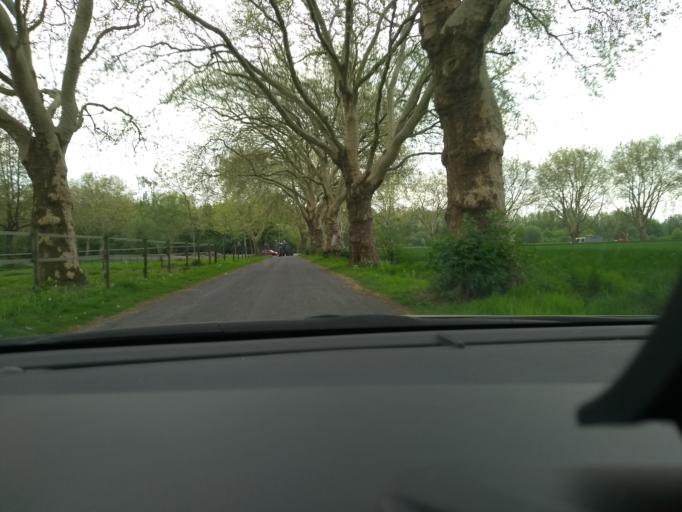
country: DE
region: North Rhine-Westphalia
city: Lunen
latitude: 51.6011
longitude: 7.5205
